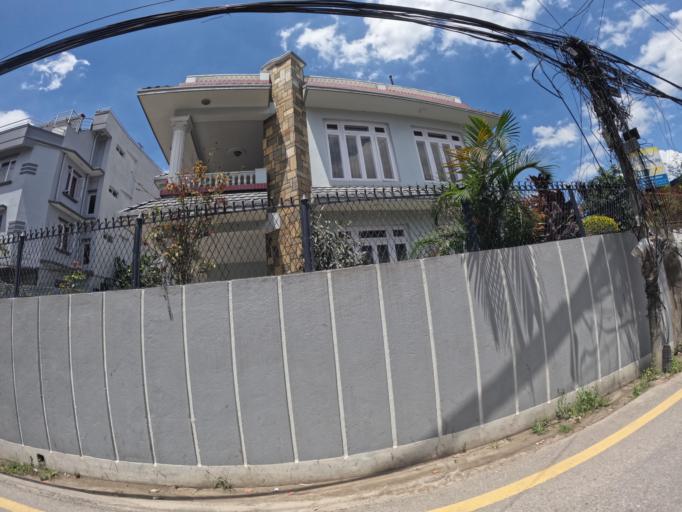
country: NP
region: Central Region
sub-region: Bagmati Zone
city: Kathmandu
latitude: 27.7390
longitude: 85.3201
